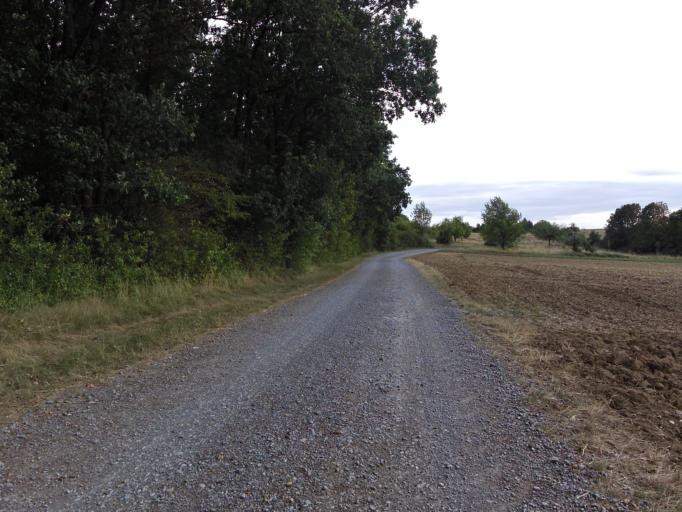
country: DE
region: Bavaria
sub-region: Regierungsbezirk Unterfranken
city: Rimpar
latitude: 49.8375
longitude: 9.9690
